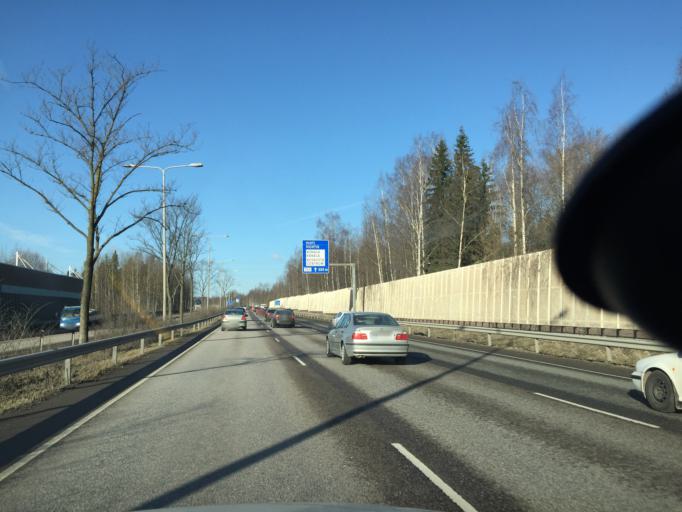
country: FI
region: Uusimaa
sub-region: Helsinki
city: Teekkarikylae
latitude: 60.2347
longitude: 24.8739
